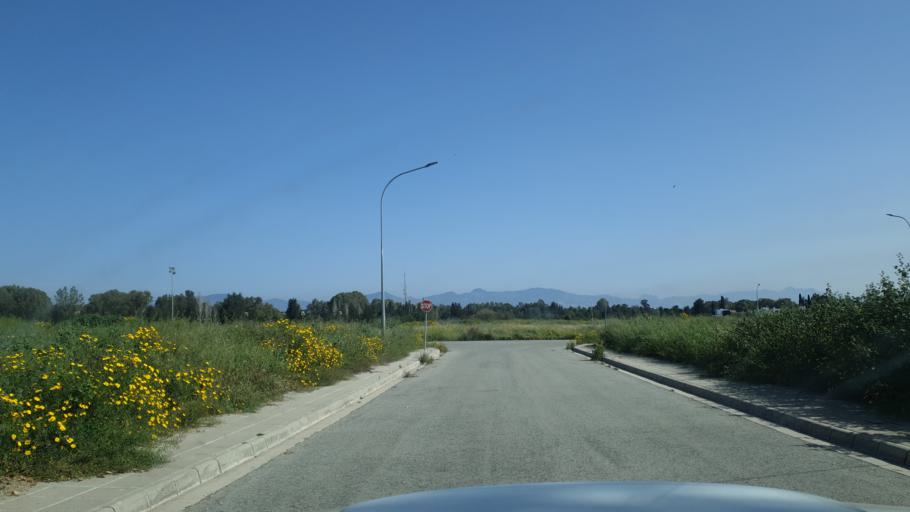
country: CY
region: Lefkosia
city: Tseri
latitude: 35.1312
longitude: 33.3184
